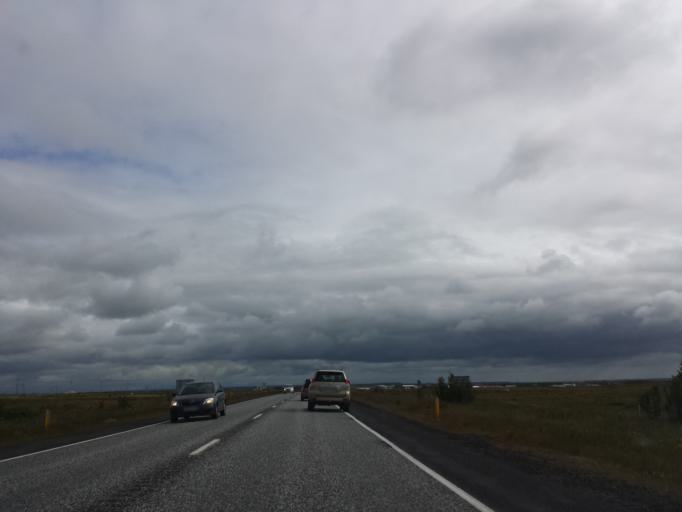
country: IS
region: South
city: Selfoss
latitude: 63.9536
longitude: -21.0369
